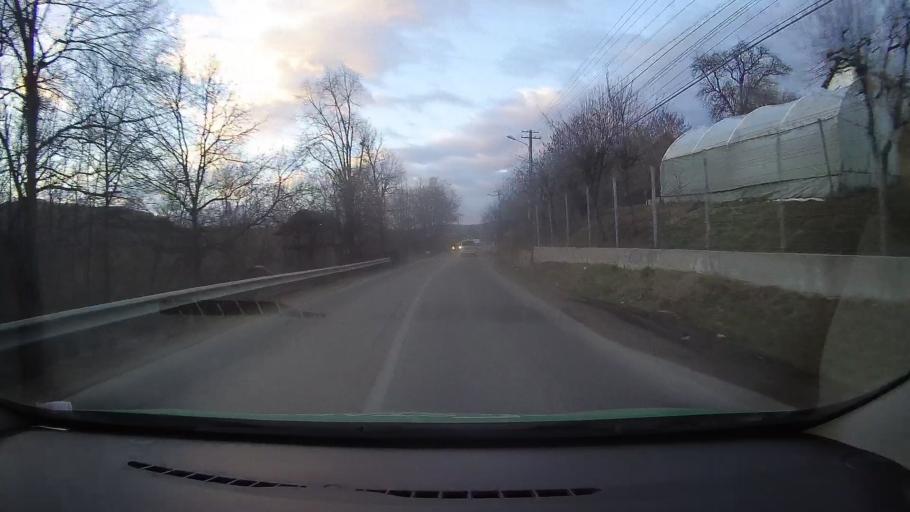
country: RO
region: Dambovita
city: Iedera de Jos
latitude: 45.0185
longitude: 25.6387
